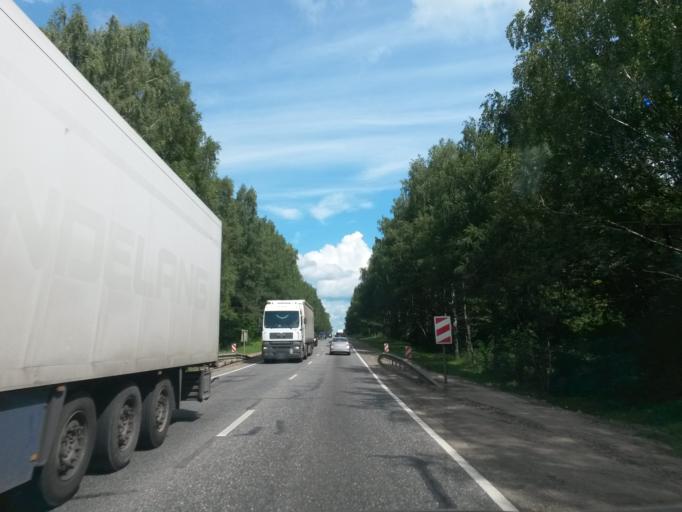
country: RU
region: Jaroslavl
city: Pereslavl'-Zalesskiy
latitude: 56.7861
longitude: 38.8848
